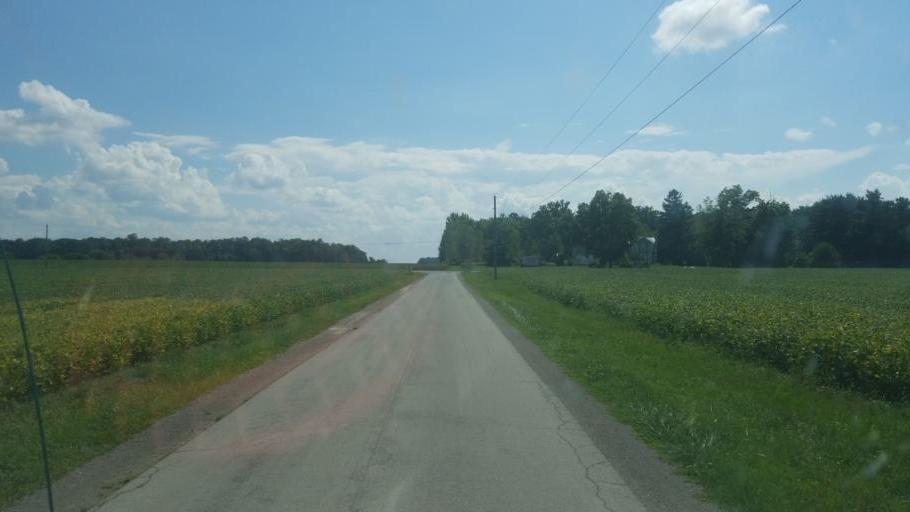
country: US
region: Ohio
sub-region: Wyandot County
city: Upper Sandusky
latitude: 40.8627
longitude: -83.3424
